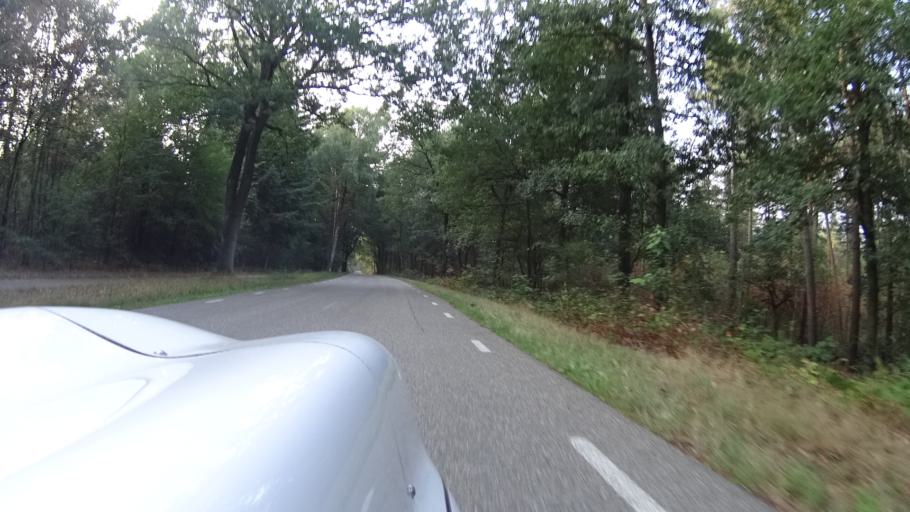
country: NL
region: Limburg
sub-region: Gemeente Venlo
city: Arcen
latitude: 51.4932
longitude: 6.2050
